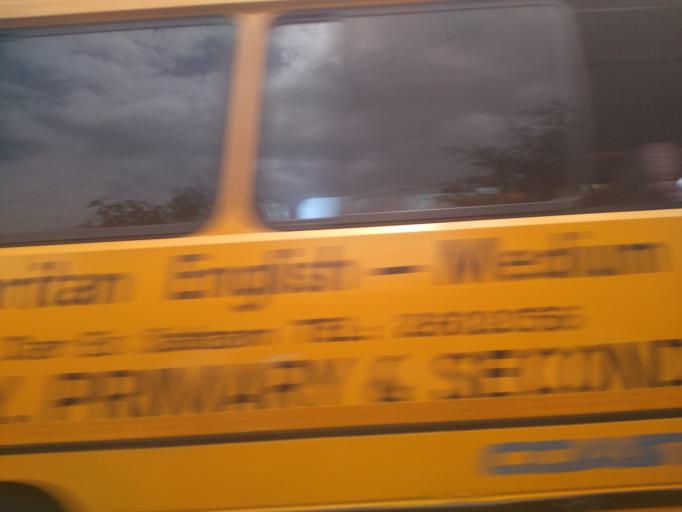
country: TZ
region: Dar es Salaam
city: Magomeni
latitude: -6.7554
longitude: 39.2803
